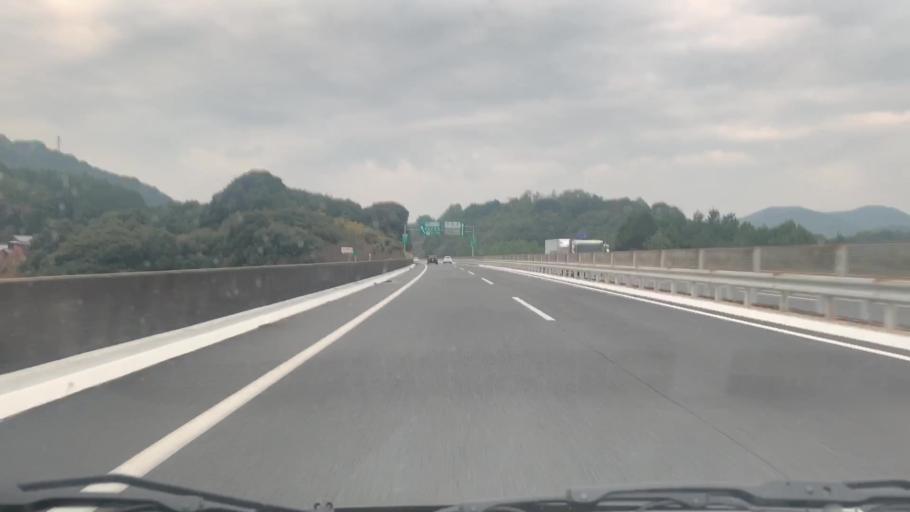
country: JP
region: Nagasaki
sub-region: Isahaya-shi
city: Isahaya
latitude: 32.8204
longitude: 129.9830
